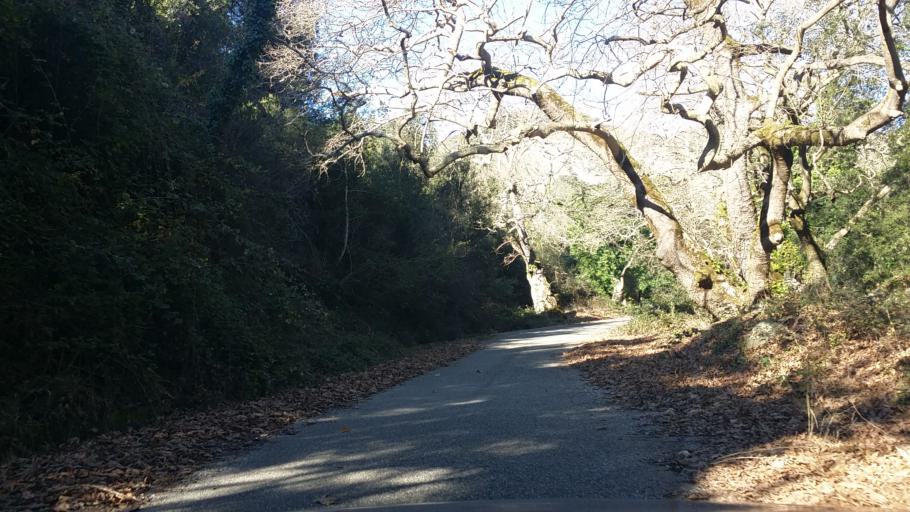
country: GR
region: West Greece
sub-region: Nomos Aitolias kai Akarnanias
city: Krikellos
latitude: 39.0111
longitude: 21.2388
